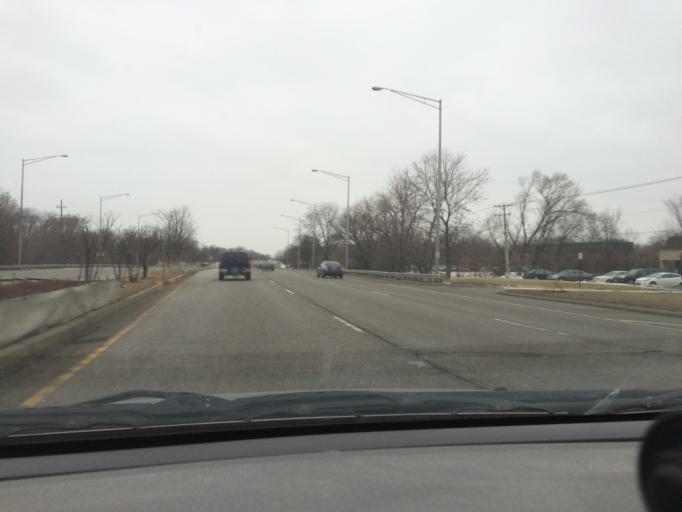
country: US
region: Illinois
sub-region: Cook County
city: Hoffman Estates
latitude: 42.0412
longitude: -88.0616
